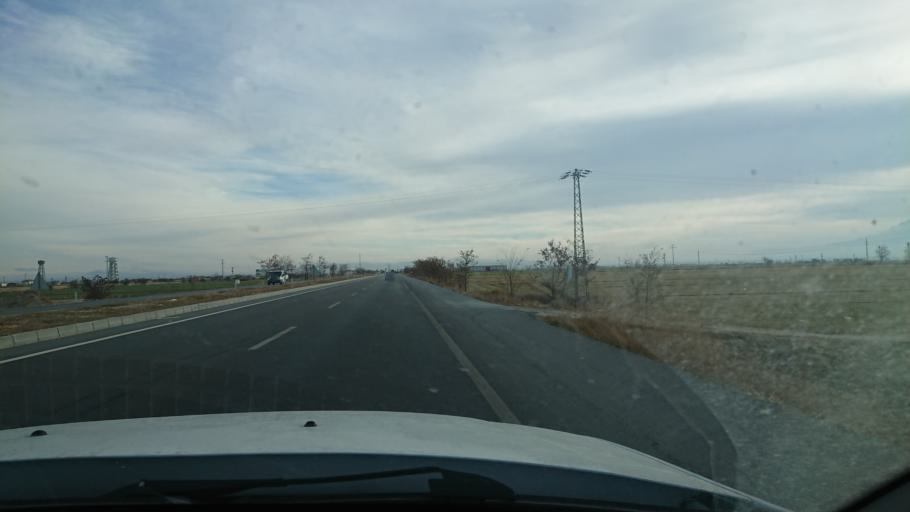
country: TR
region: Aksaray
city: Yesilova
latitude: 38.2877
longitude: 33.7453
